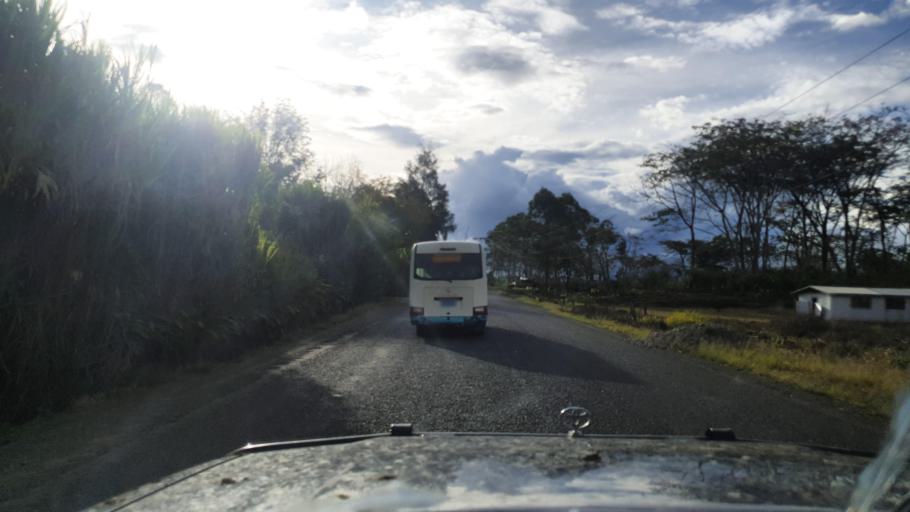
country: PG
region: Jiwaka
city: Minj
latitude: -5.8473
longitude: 144.5936
